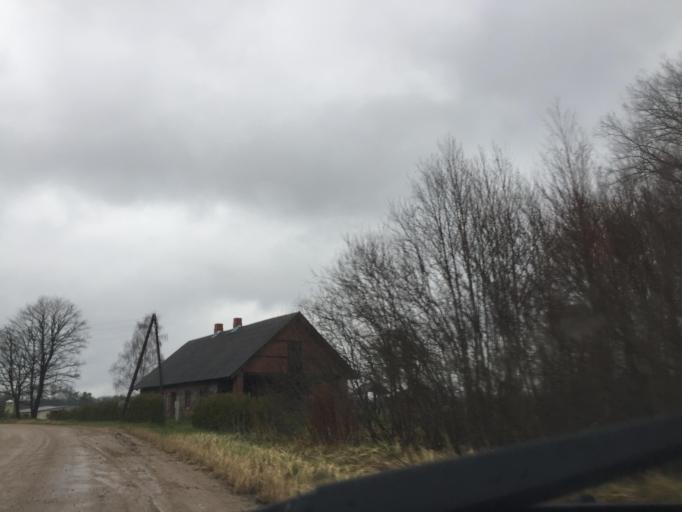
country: LV
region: Limbazu Rajons
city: Limbazi
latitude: 57.6516
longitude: 24.7772
